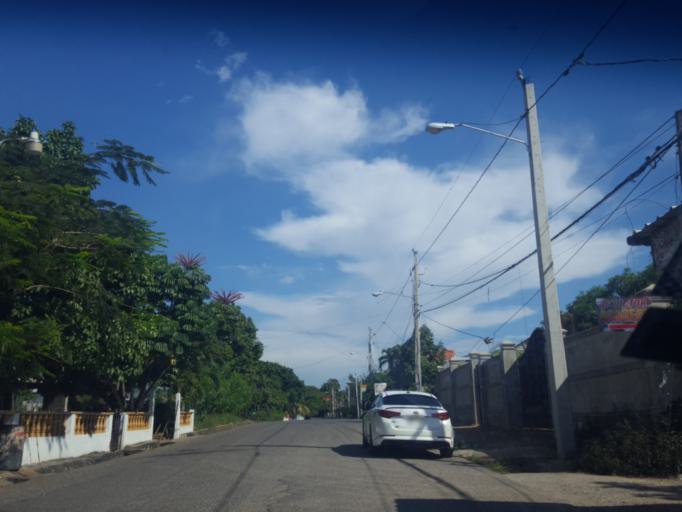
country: DO
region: Santiago
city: Licey al Medio
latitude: 19.3697
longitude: -70.6072
